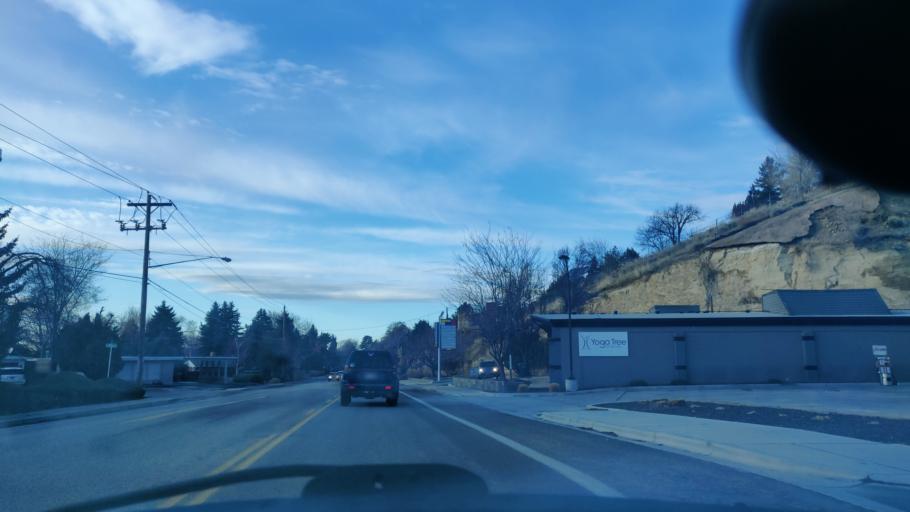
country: US
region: Idaho
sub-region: Ada County
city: Boise
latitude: 43.6406
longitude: -116.2089
